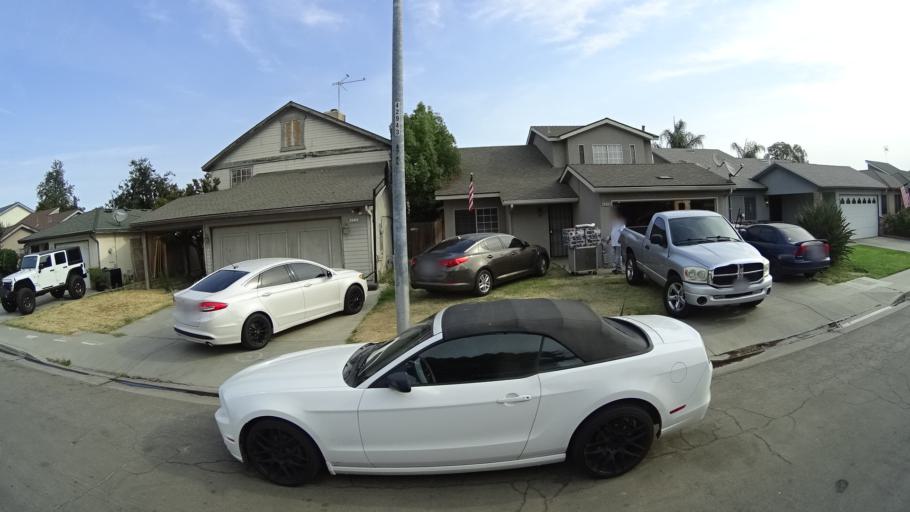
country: US
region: California
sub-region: Fresno County
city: West Park
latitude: 36.7743
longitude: -119.8693
